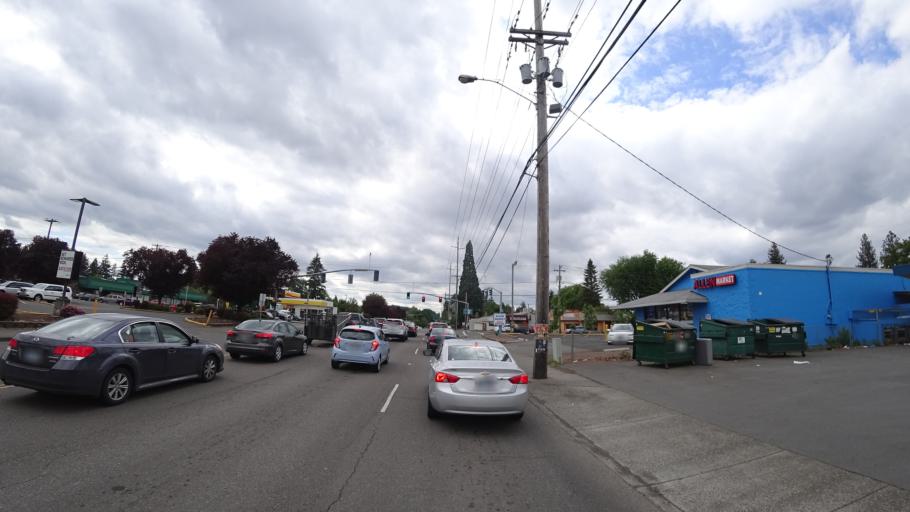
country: US
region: Oregon
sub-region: Washington County
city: Beaverton
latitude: 45.4765
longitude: -122.8048
